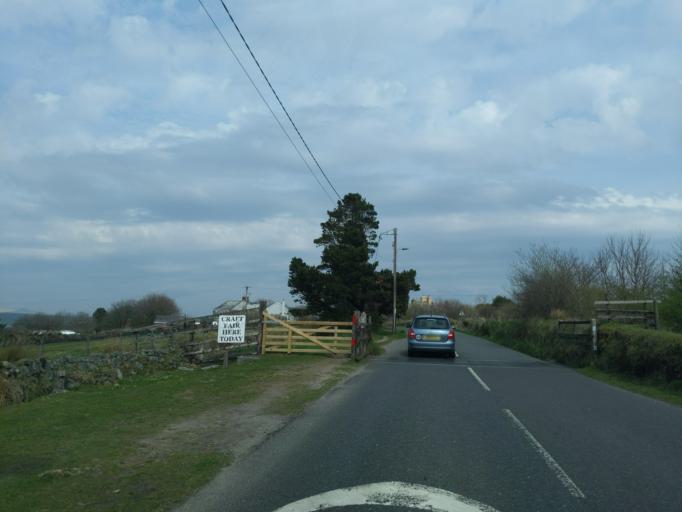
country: GB
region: England
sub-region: Devon
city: Yelverton
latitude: 50.5426
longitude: -3.9937
